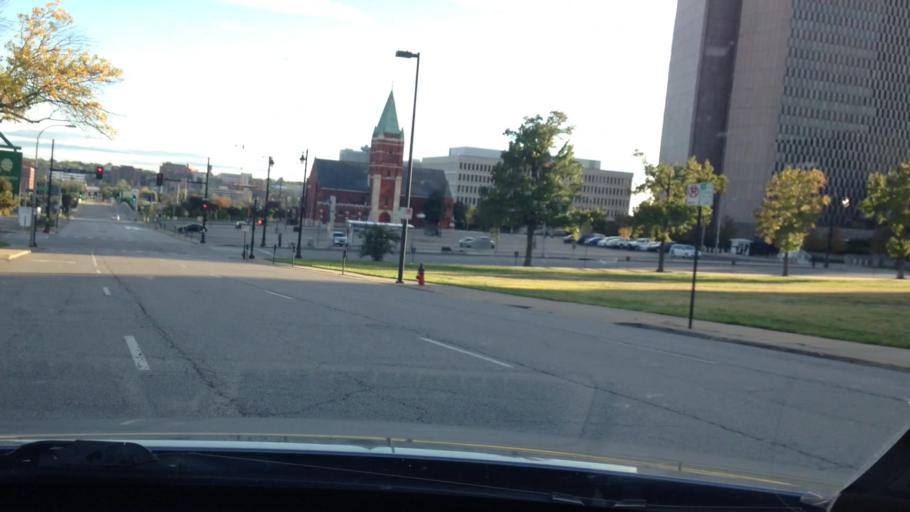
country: US
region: Missouri
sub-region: Jackson County
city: Kansas City
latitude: 39.1005
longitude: -94.5738
